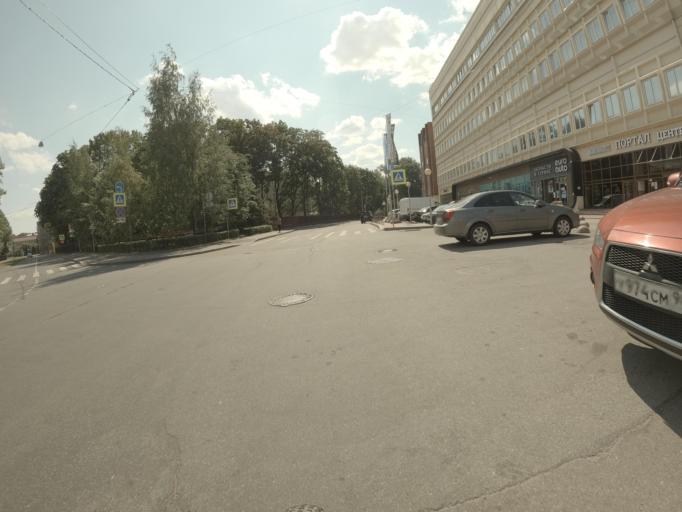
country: RU
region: St.-Petersburg
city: Admiralteisky
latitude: 59.9059
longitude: 30.2673
